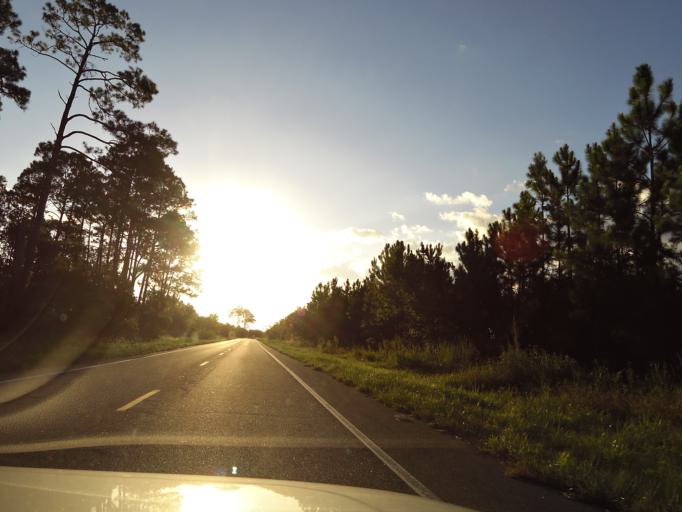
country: US
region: Florida
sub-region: Franklin County
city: Apalachicola
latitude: 29.7180
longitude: -85.0572
